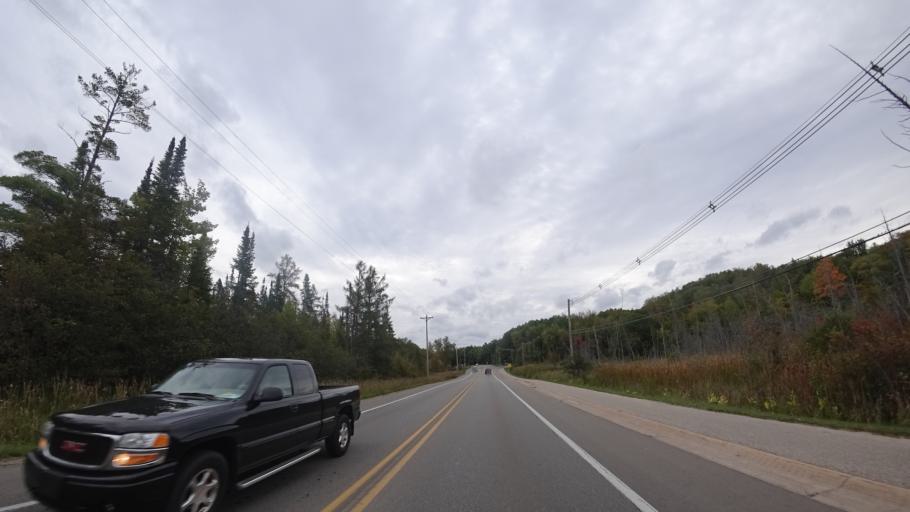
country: US
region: Michigan
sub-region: Emmet County
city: Petoskey
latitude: 45.4170
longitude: -84.9044
